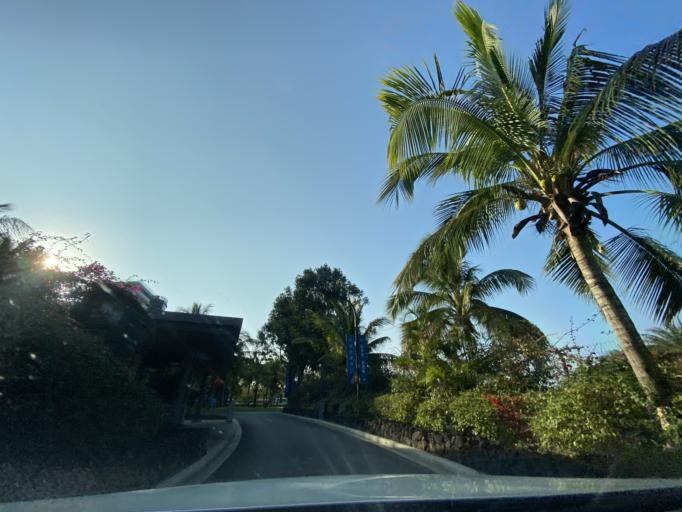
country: CN
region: Hainan
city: Xincun
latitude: 18.4195
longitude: 109.9500
